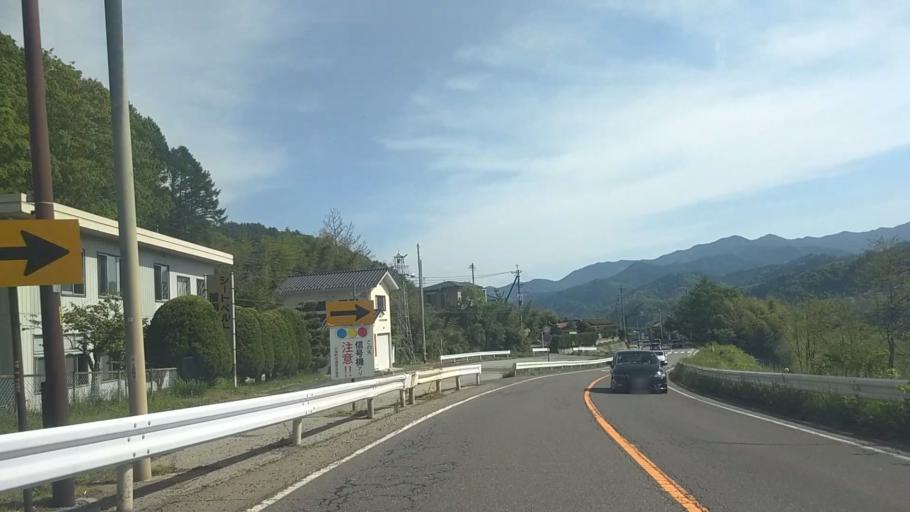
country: JP
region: Nagano
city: Saku
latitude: 36.0741
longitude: 138.4768
